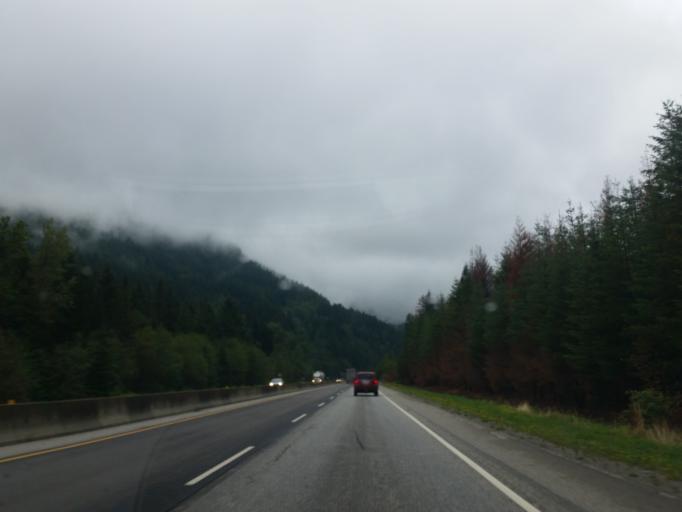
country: CA
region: British Columbia
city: Hope
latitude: 49.4717
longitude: -121.2543
